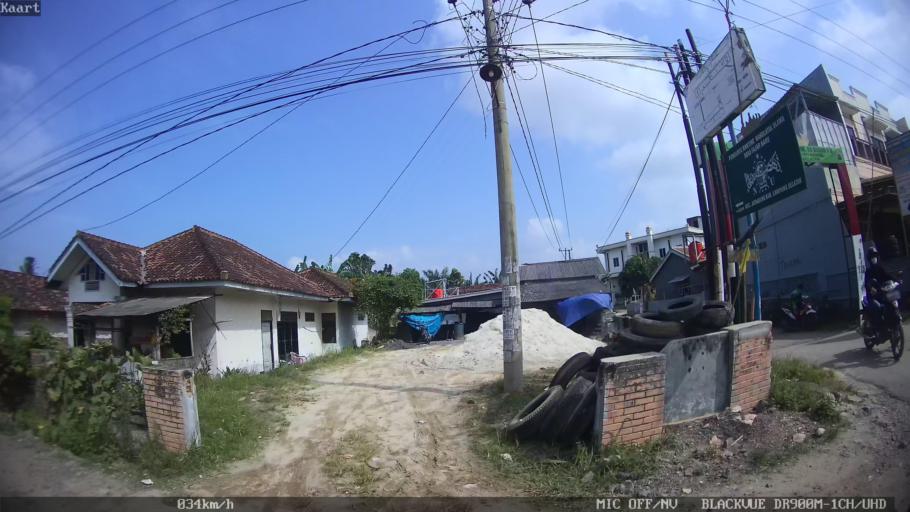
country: ID
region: Lampung
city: Kedaton
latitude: -5.3423
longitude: 105.2710
